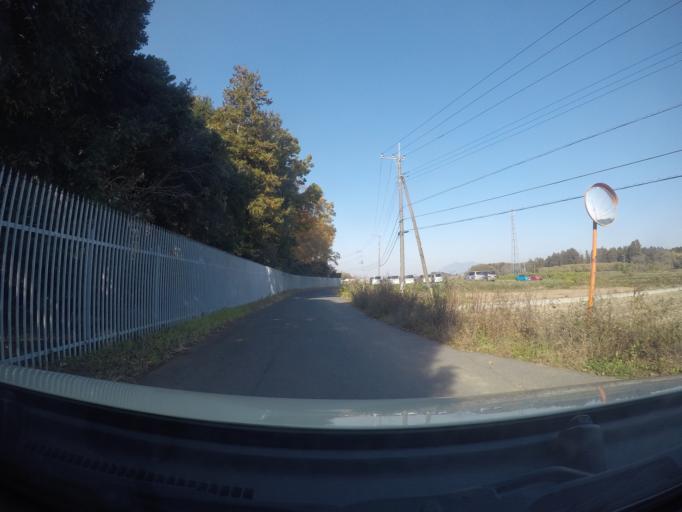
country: JP
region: Ibaraki
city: Naka
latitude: 36.1027
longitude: 140.1138
